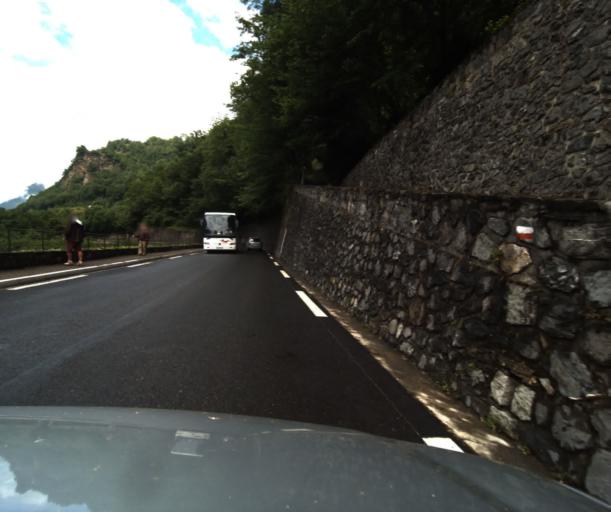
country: FR
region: Midi-Pyrenees
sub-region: Departement des Hautes-Pyrenees
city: Luz-Saint-Sauveur
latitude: 42.8585
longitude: -0.0049
